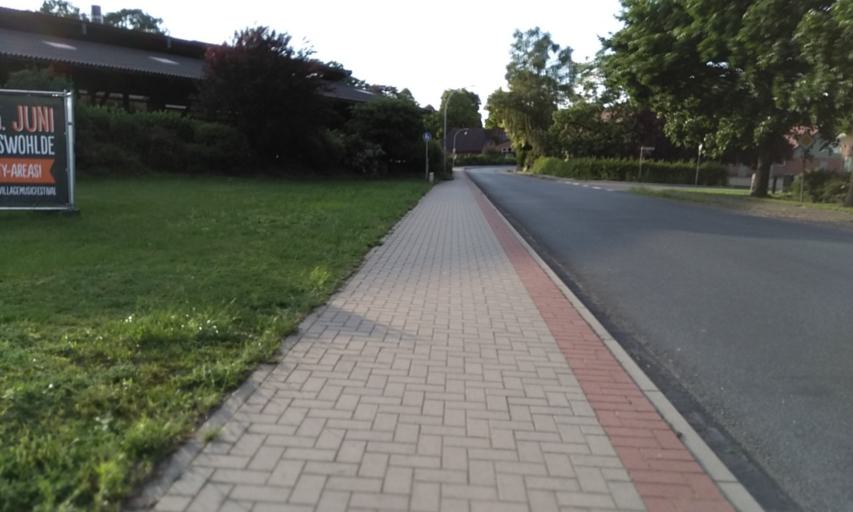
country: DE
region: Lower Saxony
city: Anderlingen
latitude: 53.3702
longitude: 9.3029
